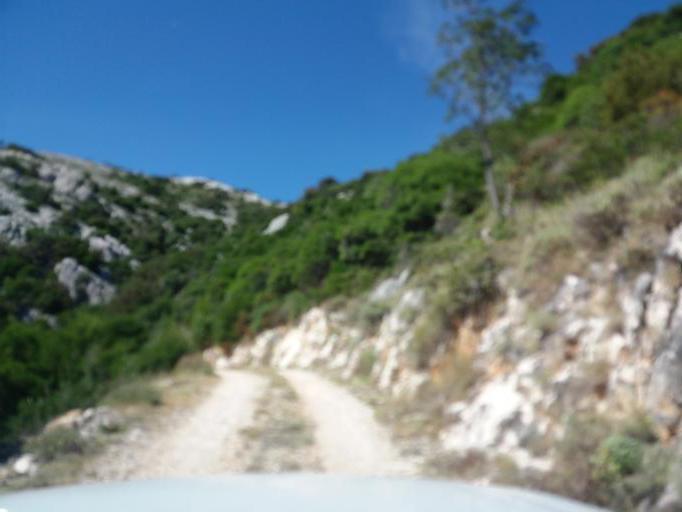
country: HR
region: Zadarska
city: Ugljan
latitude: 44.0075
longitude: 15.0366
